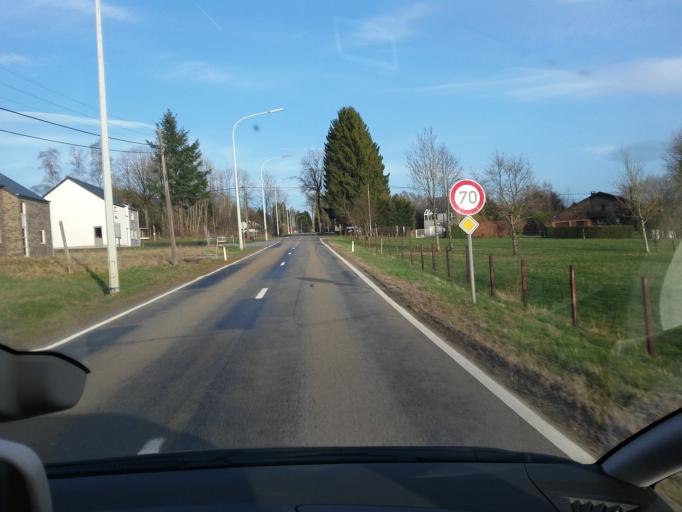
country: BE
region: Wallonia
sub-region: Province du Luxembourg
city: Libin
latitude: 50.0089
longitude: 5.2105
